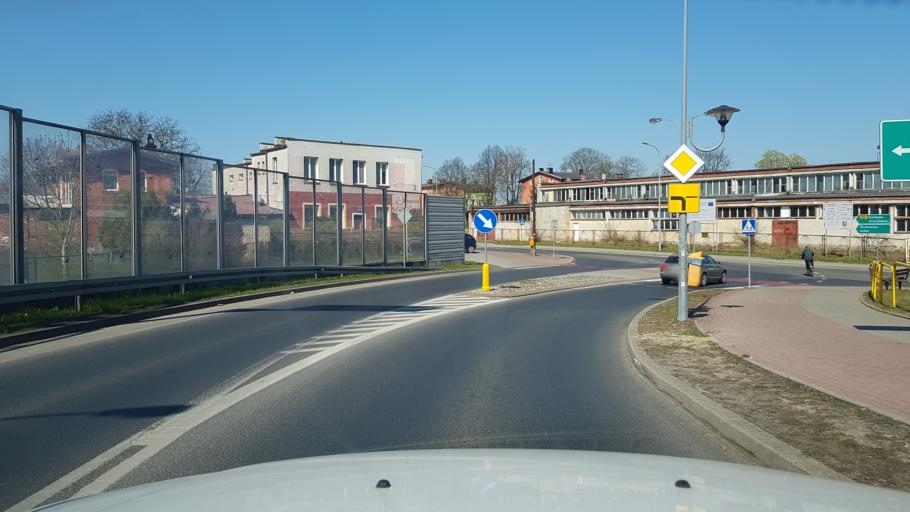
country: PL
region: West Pomeranian Voivodeship
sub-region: Powiat slawienski
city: Slawno
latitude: 54.3542
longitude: 16.6769
